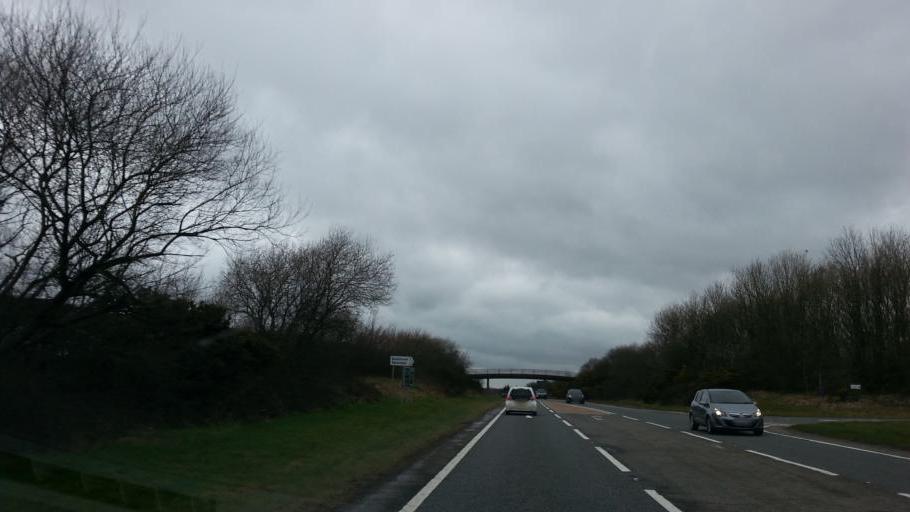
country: GB
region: England
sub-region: Devon
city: Tiverton
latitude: 50.9483
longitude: -3.5989
